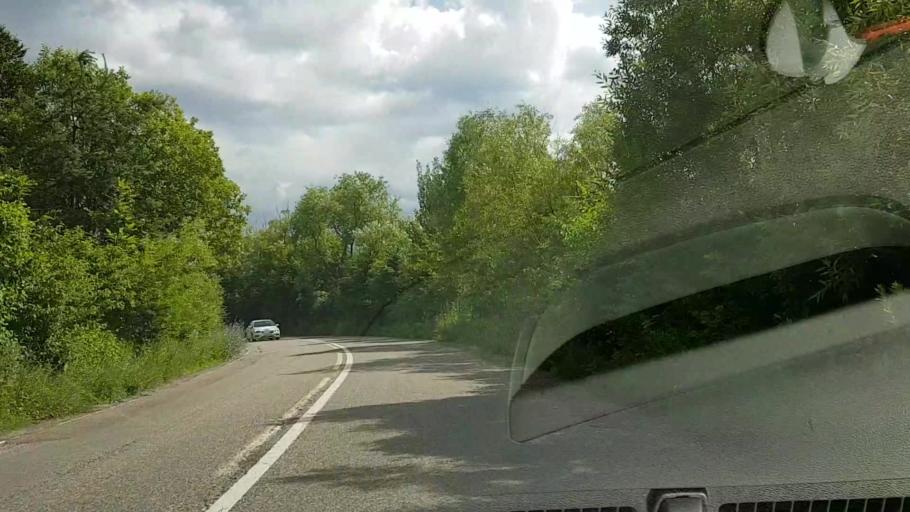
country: RO
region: Neamt
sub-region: Comuna Ceahlau
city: Ceahlau
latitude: 47.0674
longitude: 25.9607
